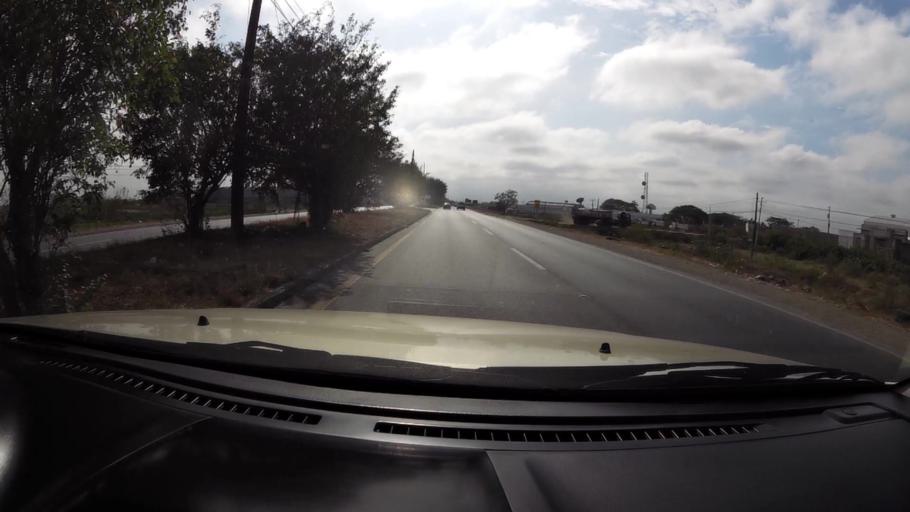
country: EC
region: Guayas
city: Eloy Alfaro
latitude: -2.1869
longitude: -79.8048
